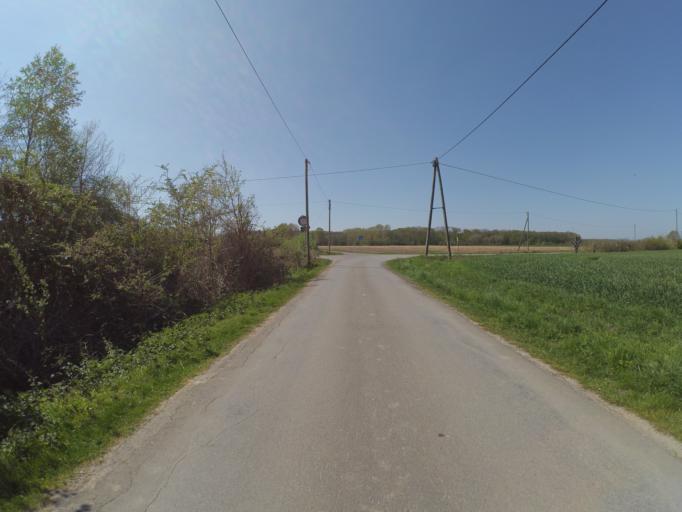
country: DE
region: North Rhine-Westphalia
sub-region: Regierungsbezirk Munster
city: Ascheberg
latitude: 51.8057
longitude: 7.5949
